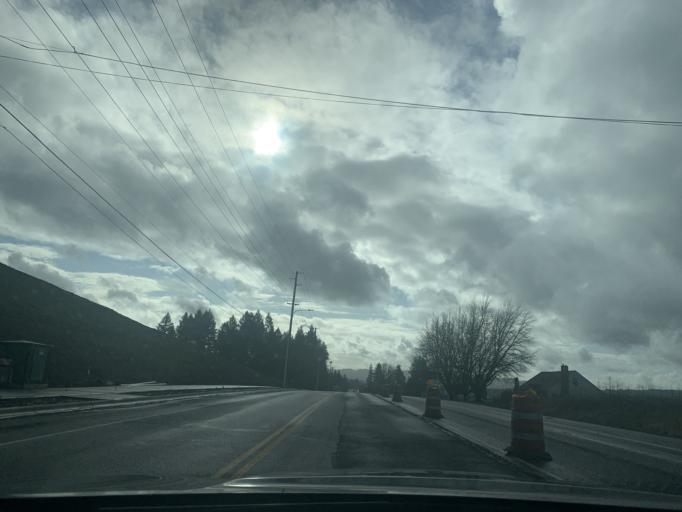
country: US
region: Oregon
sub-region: Washington County
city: King City
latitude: 45.4103
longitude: -122.8516
